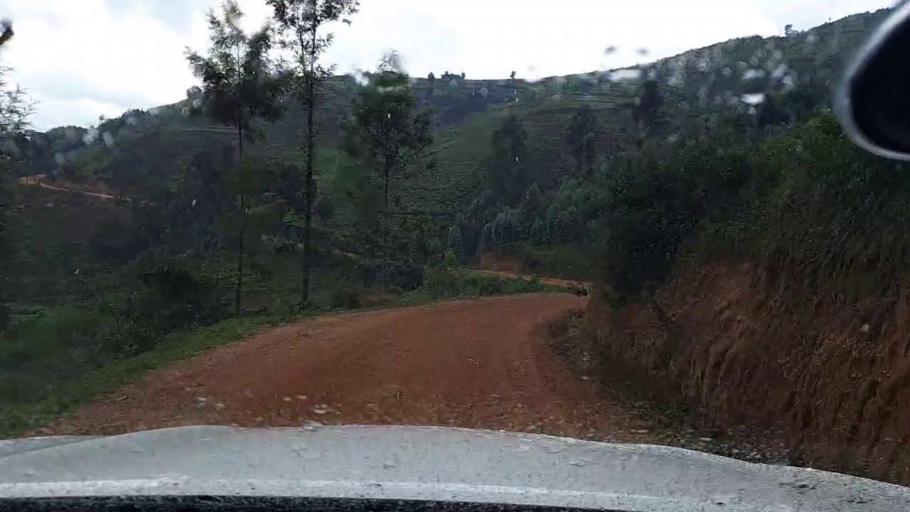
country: RW
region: Western Province
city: Kibuye
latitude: -2.1515
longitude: 29.4283
